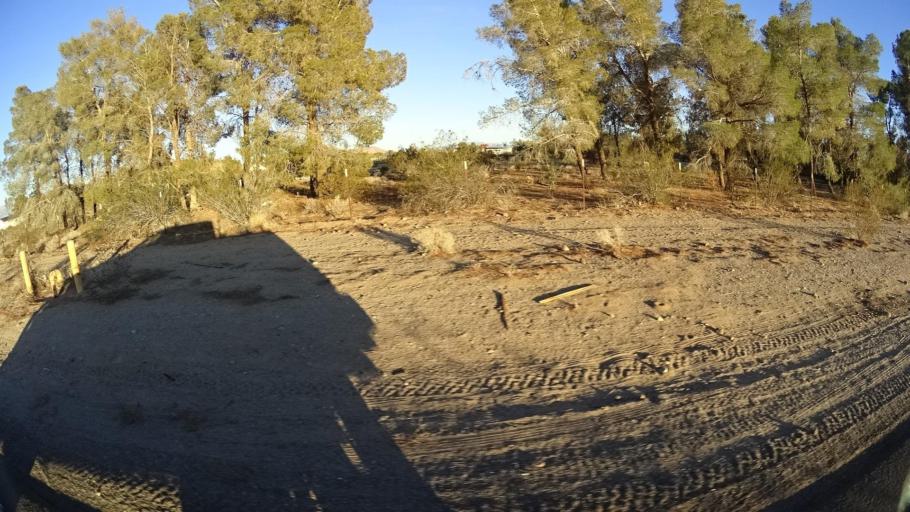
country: US
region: California
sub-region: Kern County
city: Ridgecrest
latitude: 35.6403
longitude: -117.7055
